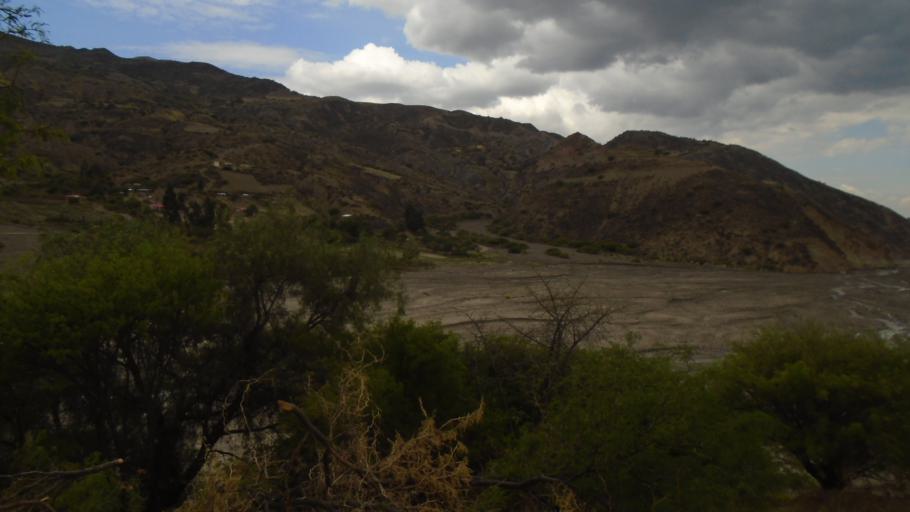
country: BO
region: Cochabamba
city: Colchani
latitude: -17.5172
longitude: -66.6179
